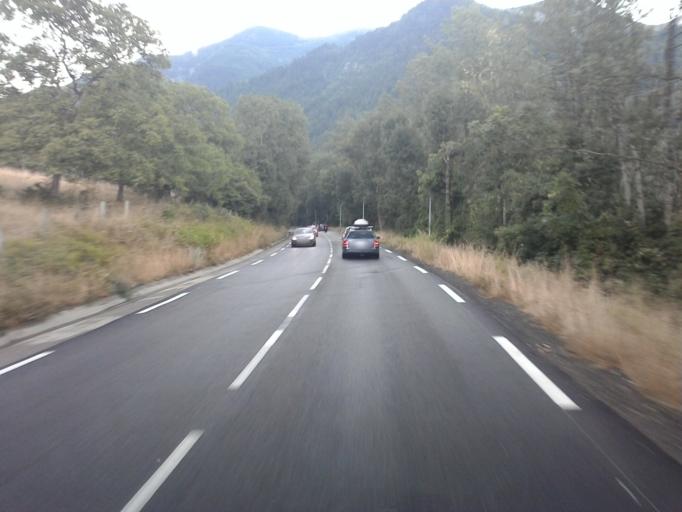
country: FR
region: Rhone-Alpes
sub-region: Departement de l'Isere
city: La Mure
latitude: 44.8234
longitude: 5.9453
